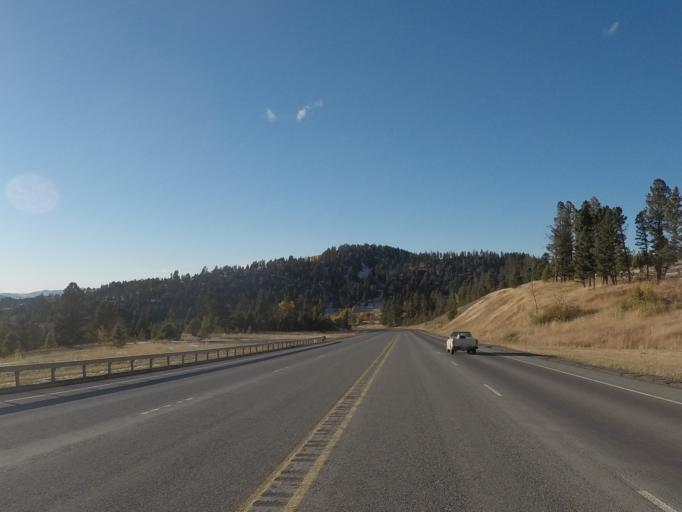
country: US
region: Montana
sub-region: Lewis and Clark County
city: Helena West Side
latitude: 46.5583
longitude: -112.3309
